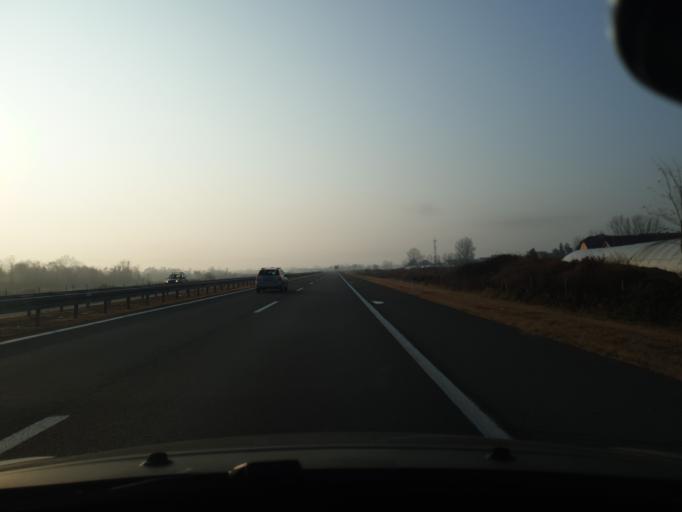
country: RS
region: Central Serbia
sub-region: Jablanicki Okrug
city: Leskovac
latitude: 42.9903
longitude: 22.0270
